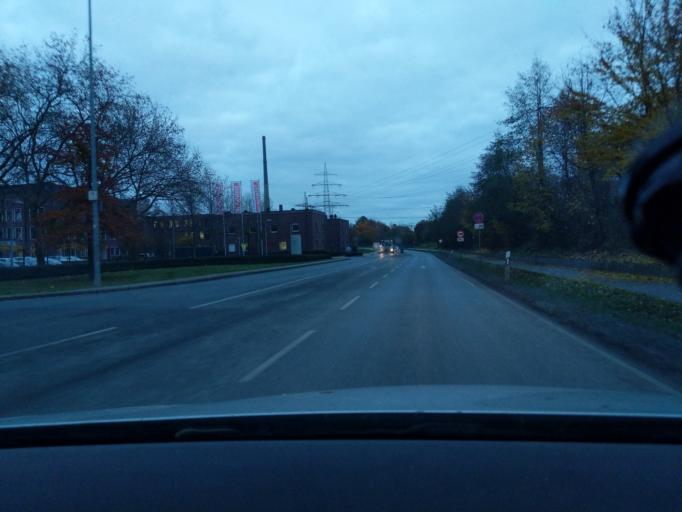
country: DE
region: North Rhine-Westphalia
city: Waltrop
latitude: 51.6162
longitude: 7.4642
